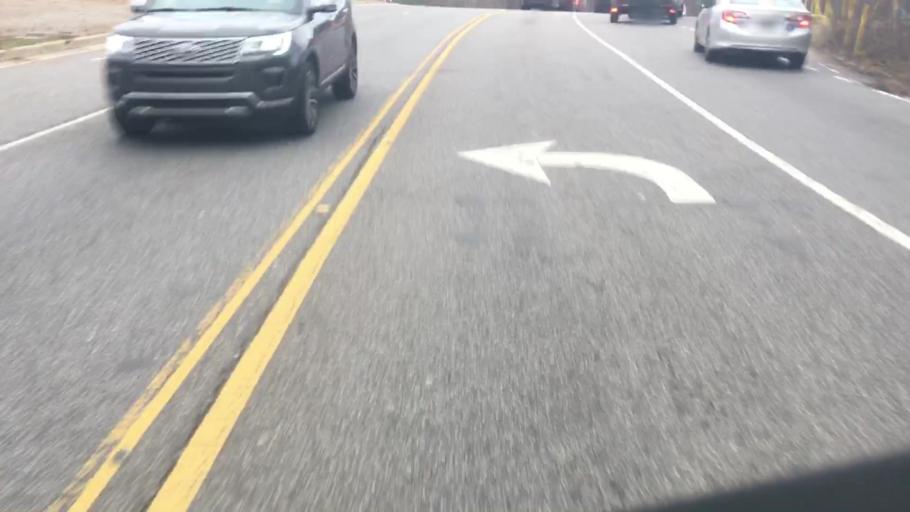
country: US
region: Alabama
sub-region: Jefferson County
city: Cahaba Heights
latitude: 33.4619
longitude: -86.7576
